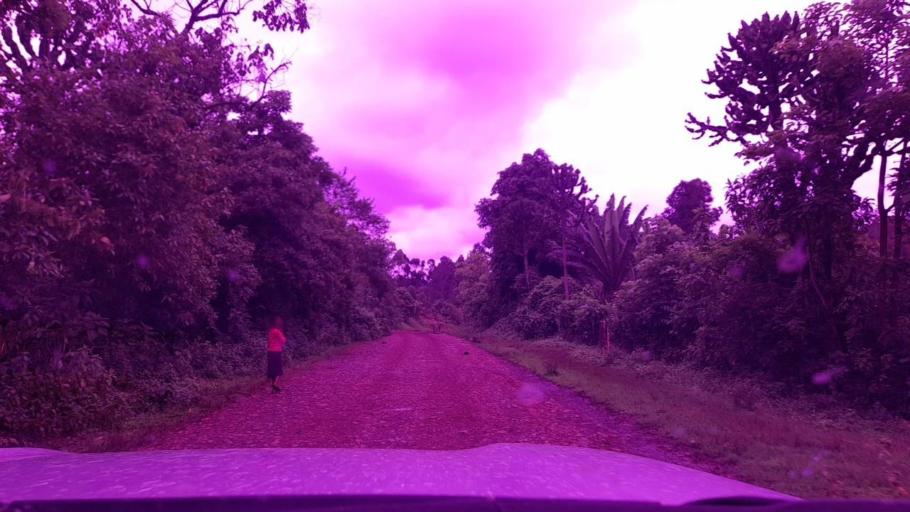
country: ET
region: Southern Nations, Nationalities, and People's Region
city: Tippi
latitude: 7.5687
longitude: 35.7850
